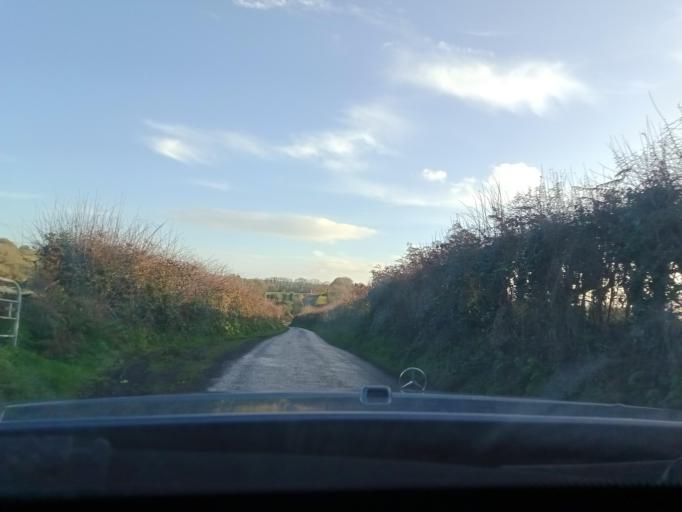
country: IE
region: Munster
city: Carrick-on-Suir
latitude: 52.4387
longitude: -7.4035
